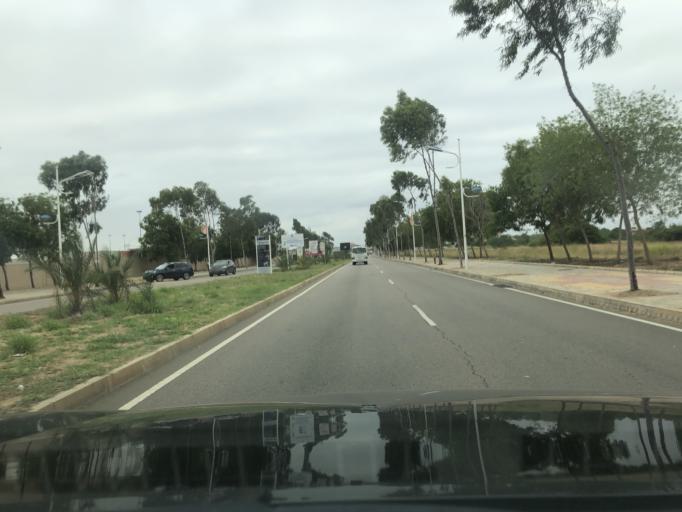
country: AO
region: Luanda
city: Luanda
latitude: -8.9913
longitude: 13.2861
